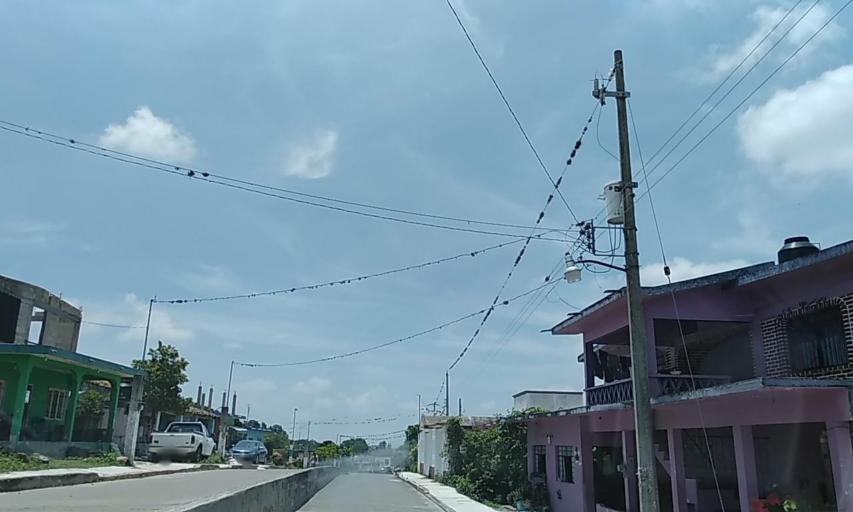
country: MX
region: Veracruz
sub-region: Emiliano Zapata
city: Dos Rios
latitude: 19.4400
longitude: -96.7555
